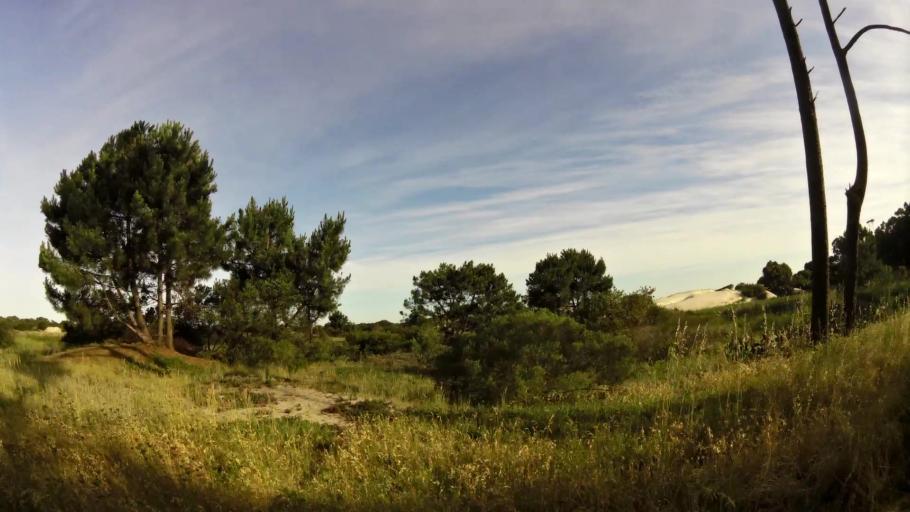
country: UY
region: Canelones
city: Atlantida
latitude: -34.7915
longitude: -55.8546
